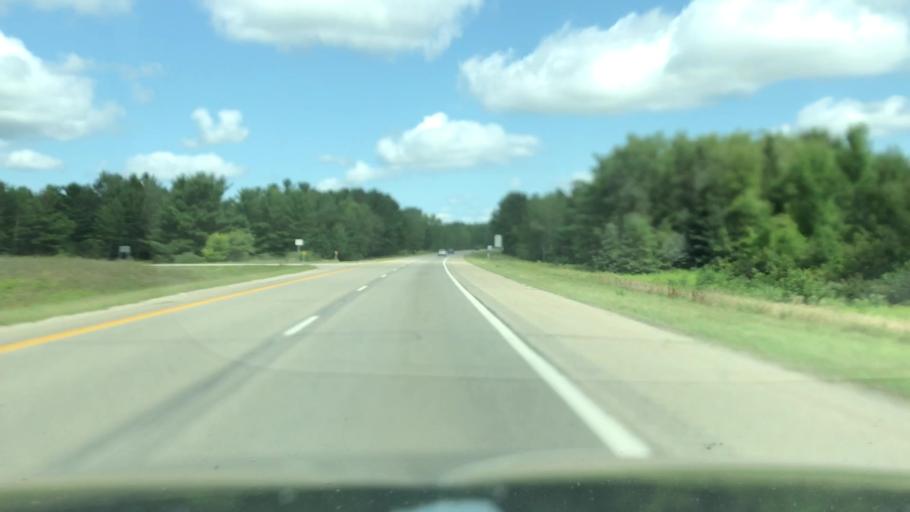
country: US
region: Michigan
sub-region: Mecosta County
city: Big Rapids
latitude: 43.6958
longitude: -85.5250
